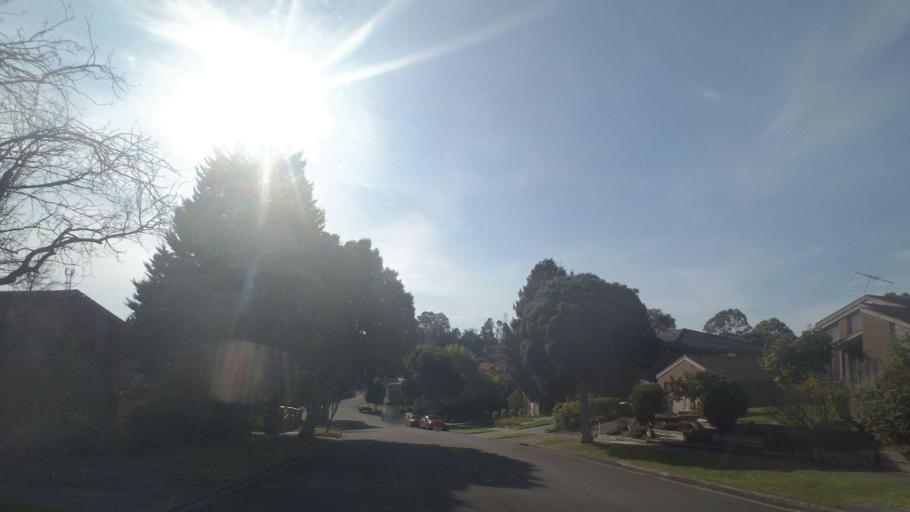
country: AU
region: Victoria
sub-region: Manningham
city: Doncaster East
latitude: -37.7710
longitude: 145.1475
